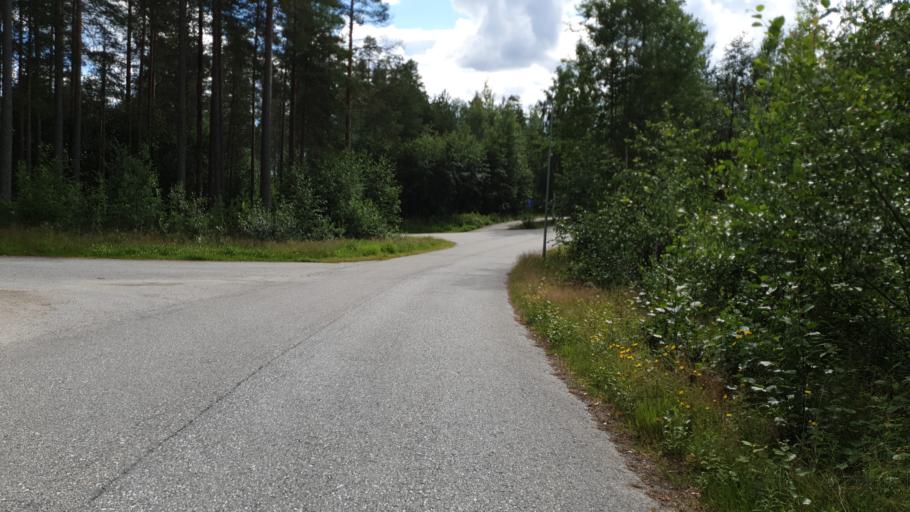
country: FI
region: Kainuu
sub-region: Kehys-Kainuu
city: Kuhmo
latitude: 64.1260
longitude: 29.5542
